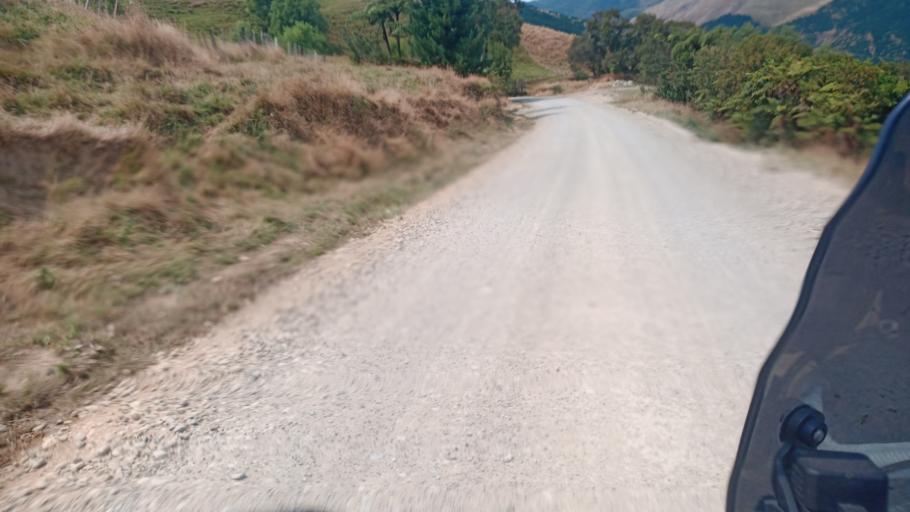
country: NZ
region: Bay of Plenty
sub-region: Opotiki District
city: Opotiki
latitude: -37.6575
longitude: 178.1291
